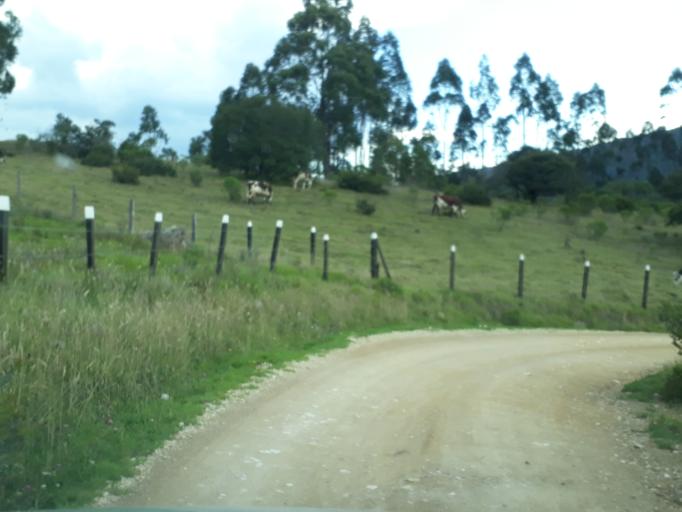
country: CO
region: Cundinamarca
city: Lenguazaque
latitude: 5.2622
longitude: -73.6938
